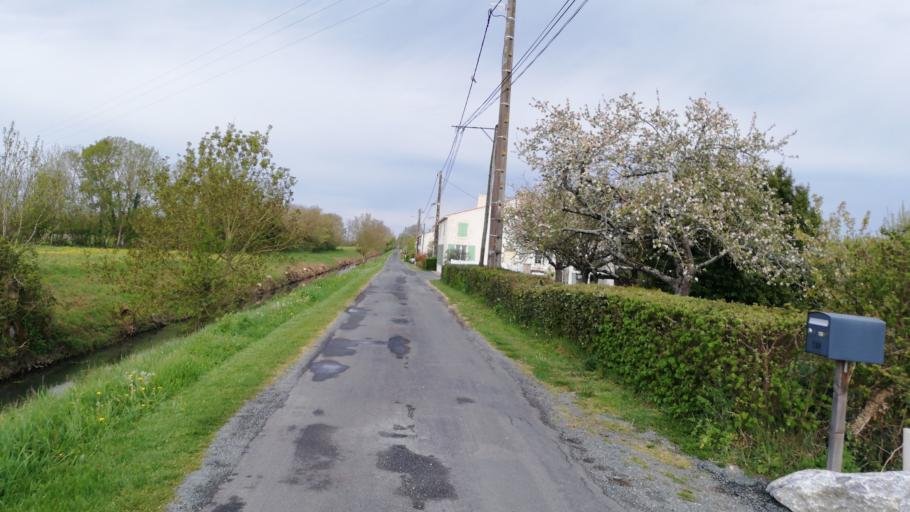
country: FR
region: Pays de la Loire
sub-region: Departement de la Vendee
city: Maillezais
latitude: 46.3279
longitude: -0.7155
